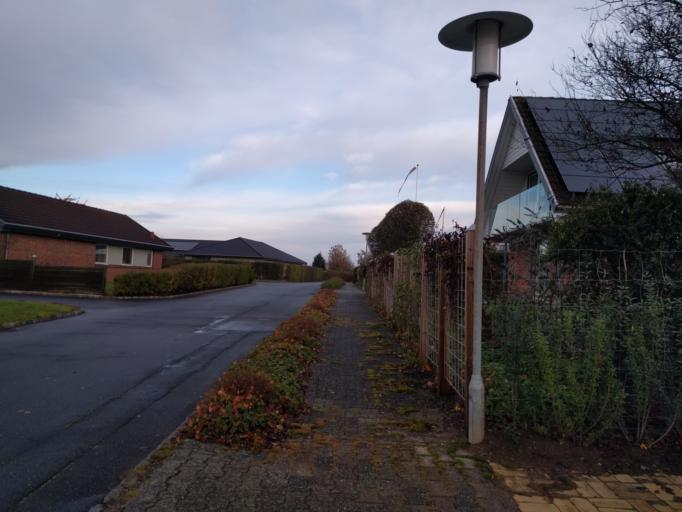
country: DK
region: South Denmark
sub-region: Fredericia Kommune
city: Snoghoj
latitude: 55.5369
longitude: 9.7287
